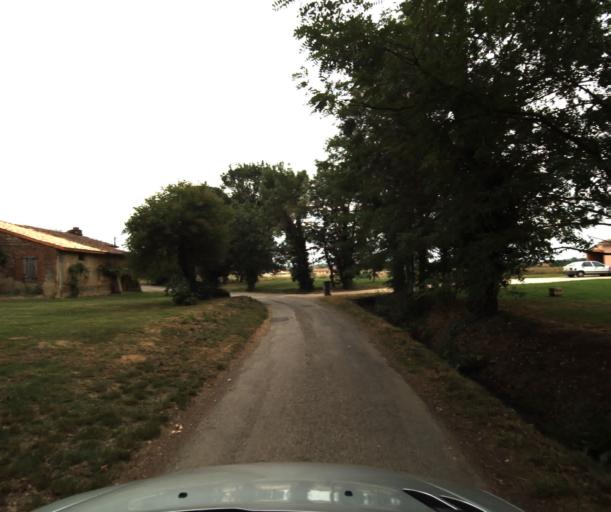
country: FR
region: Midi-Pyrenees
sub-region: Departement de la Haute-Garonne
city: Lacasse
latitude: 43.4224
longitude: 1.2713
